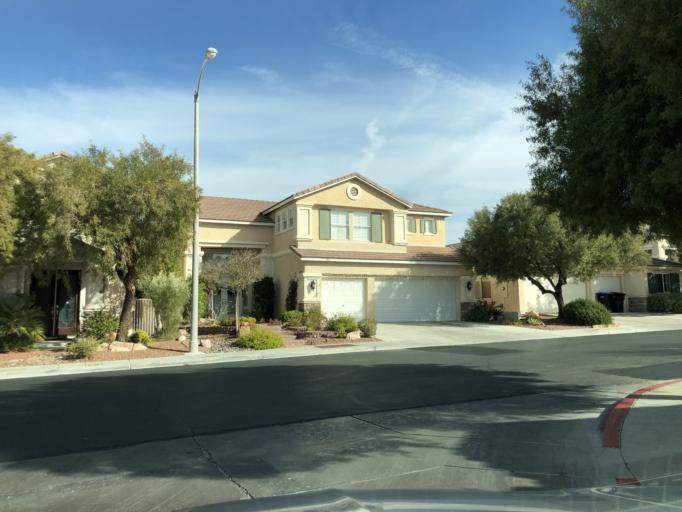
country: US
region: Nevada
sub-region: Clark County
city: Whitney
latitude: 36.0147
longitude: -115.0886
